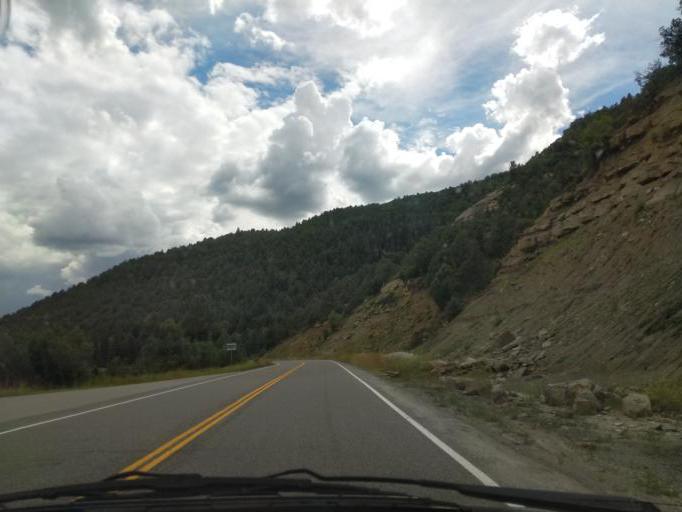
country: US
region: Colorado
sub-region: Delta County
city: Paonia
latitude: 39.0206
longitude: -107.3628
